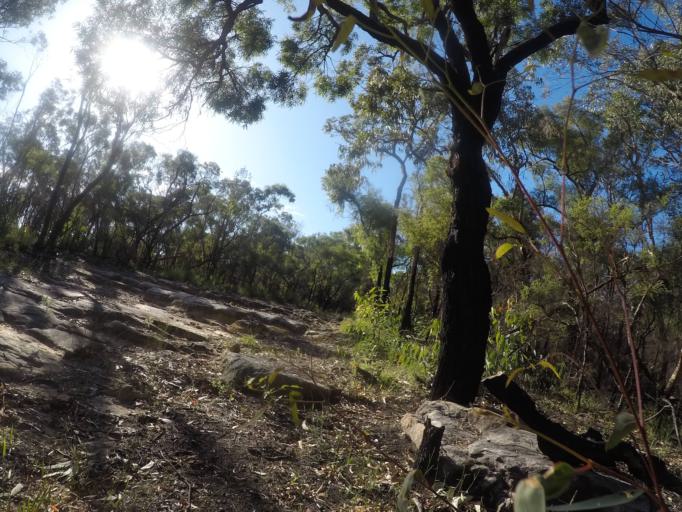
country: AU
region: New South Wales
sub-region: Hornsby Shire
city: Glenorie
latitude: -33.3420
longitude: 151.0601
